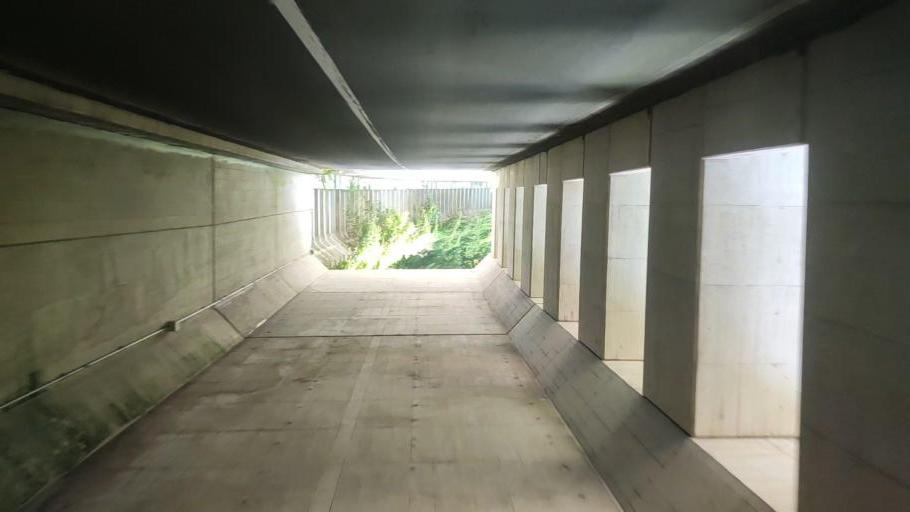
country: JP
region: Fukui
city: Ono
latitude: 35.8572
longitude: 136.4669
